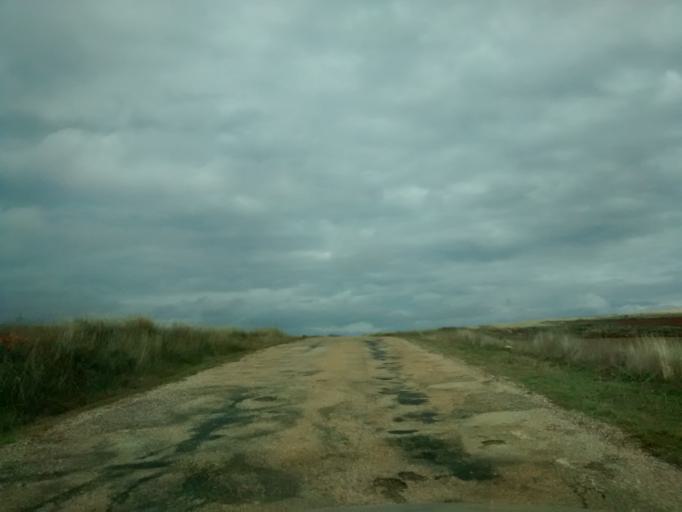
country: ES
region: Aragon
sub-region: Provincia de Zaragoza
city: Used
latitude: 41.0038
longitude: -1.5882
